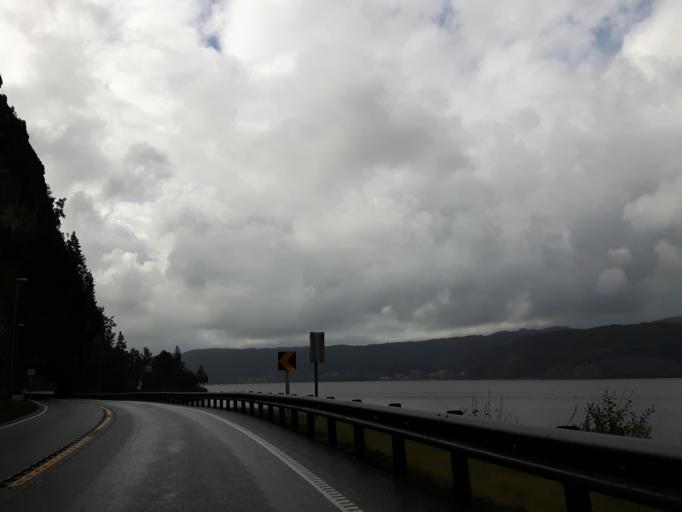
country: NO
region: Rogaland
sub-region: Lund
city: Moi
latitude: 58.4370
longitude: 6.6042
